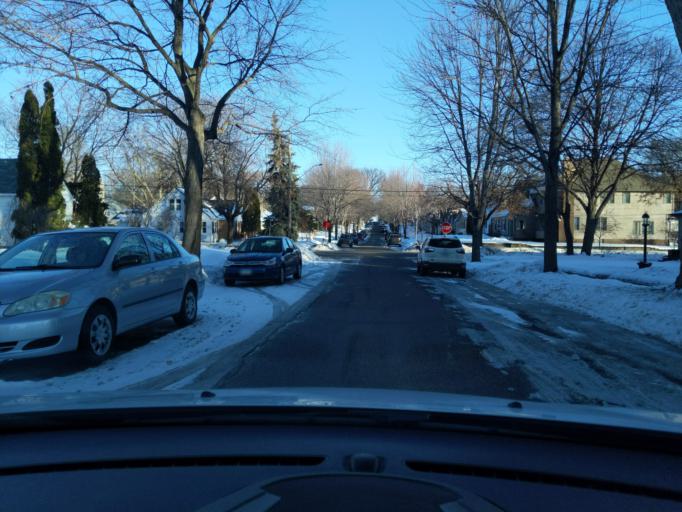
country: US
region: Minnesota
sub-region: Hennepin County
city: Richfield
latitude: 44.9085
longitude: -93.2512
